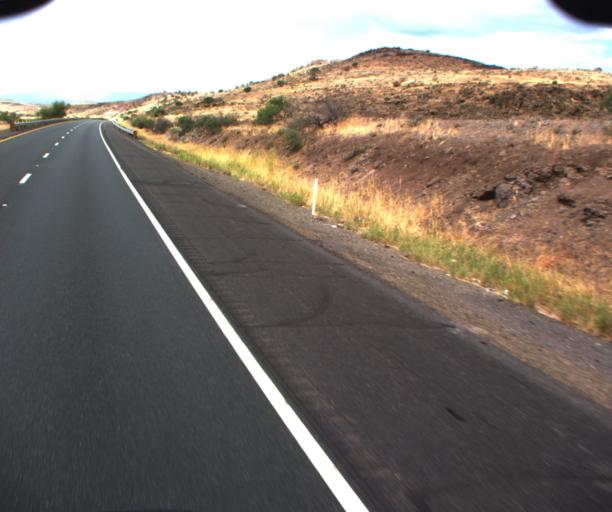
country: US
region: Arizona
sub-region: Yavapai County
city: Cordes Lakes
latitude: 34.4643
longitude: -112.0286
